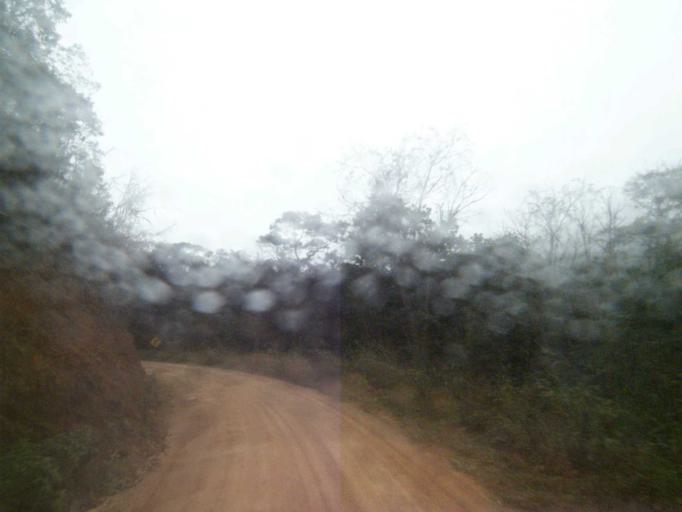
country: BR
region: Santa Catarina
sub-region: Anitapolis
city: Anitapolis
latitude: -27.8580
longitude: -49.1328
